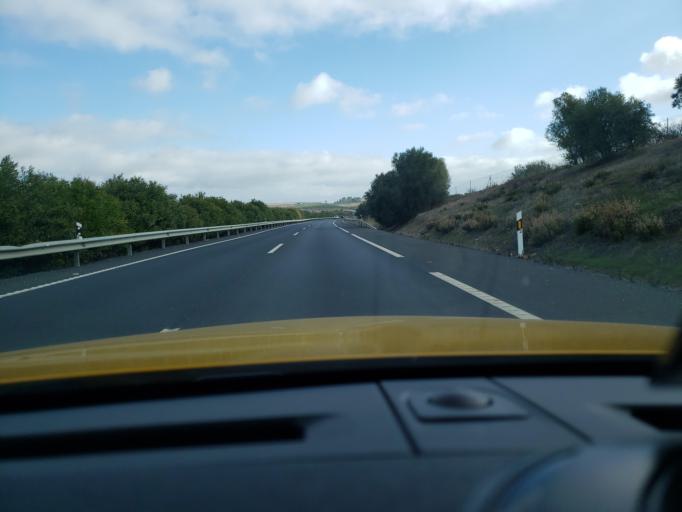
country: ES
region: Andalusia
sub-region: Provincia de Huelva
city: Niebla
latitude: 37.3424
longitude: -6.6552
